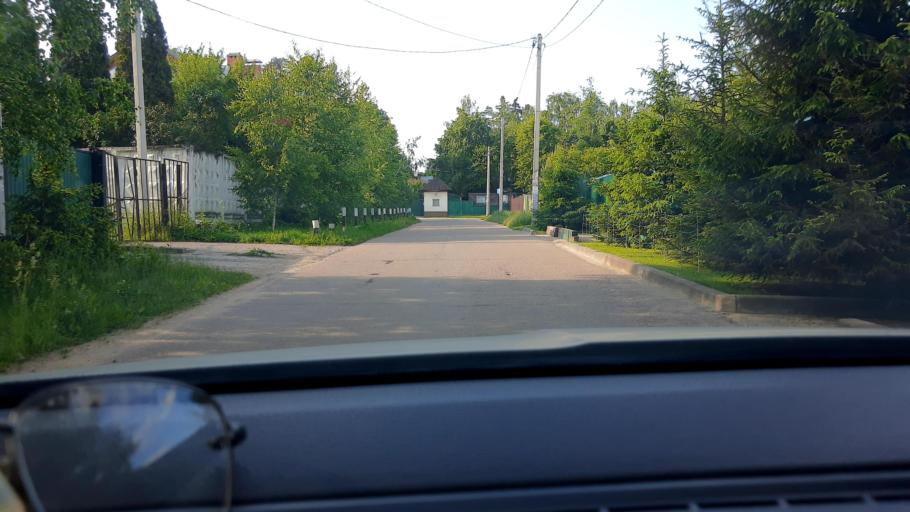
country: RU
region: Moscow
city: Novo-Peredelkino
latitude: 55.6721
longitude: 37.3197
